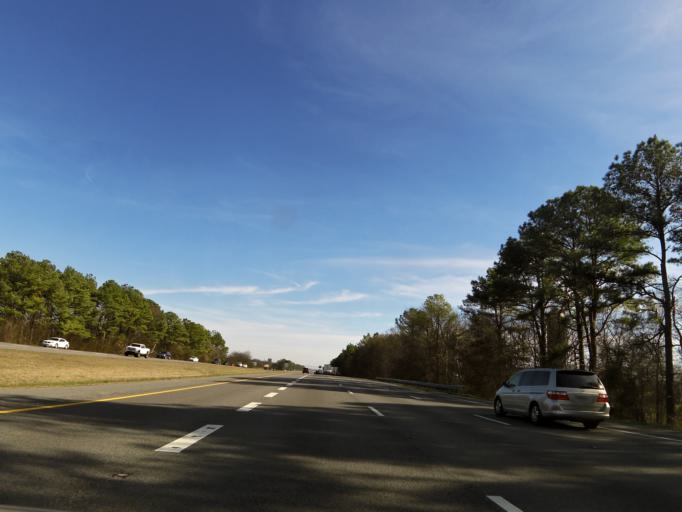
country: US
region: Tennessee
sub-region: Rutherford County
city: Smyrna
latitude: 35.9041
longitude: -86.4982
